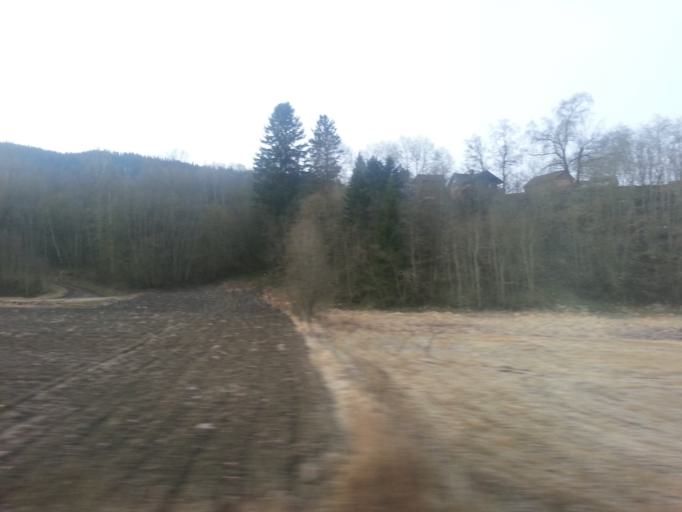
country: NO
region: Sor-Trondelag
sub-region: Melhus
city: Lundamo
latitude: 63.1625
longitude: 10.2944
